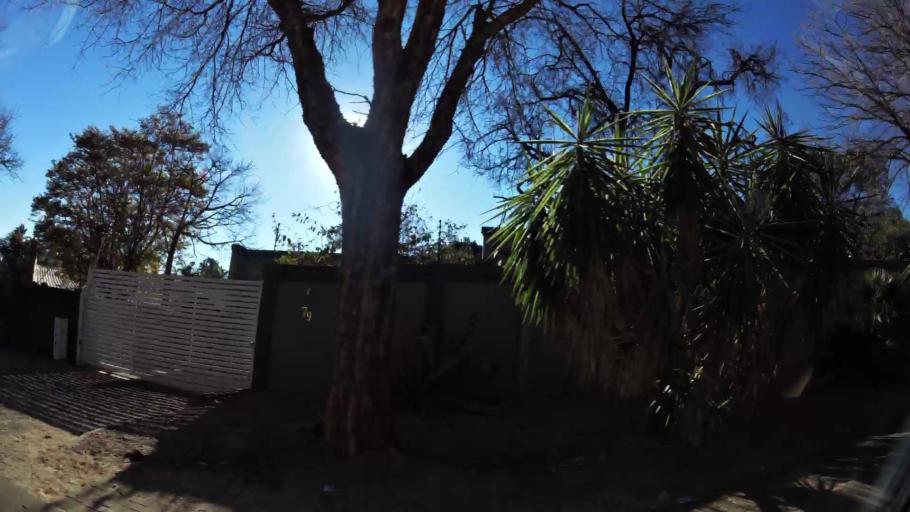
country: ZA
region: Limpopo
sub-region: Capricorn District Municipality
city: Polokwane
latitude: -23.8929
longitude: 29.4851
